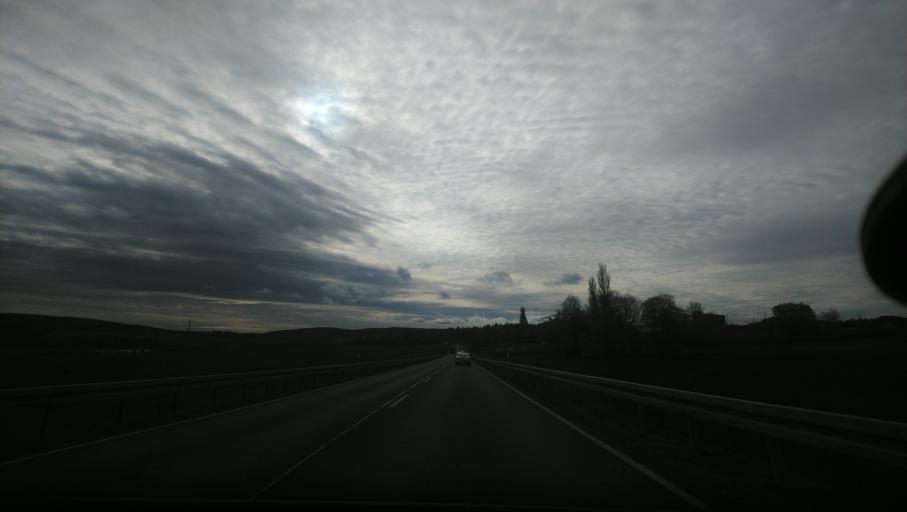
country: DE
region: Saxony
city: Dorfchemnitz
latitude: 50.6620
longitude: 12.8091
